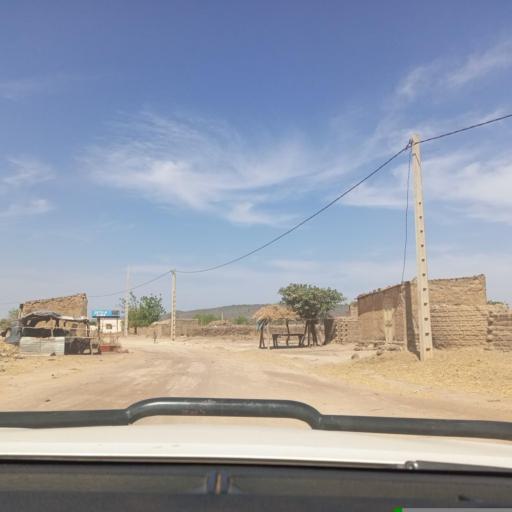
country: ML
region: Koulikoro
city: Kati
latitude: 12.8021
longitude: -8.2477
